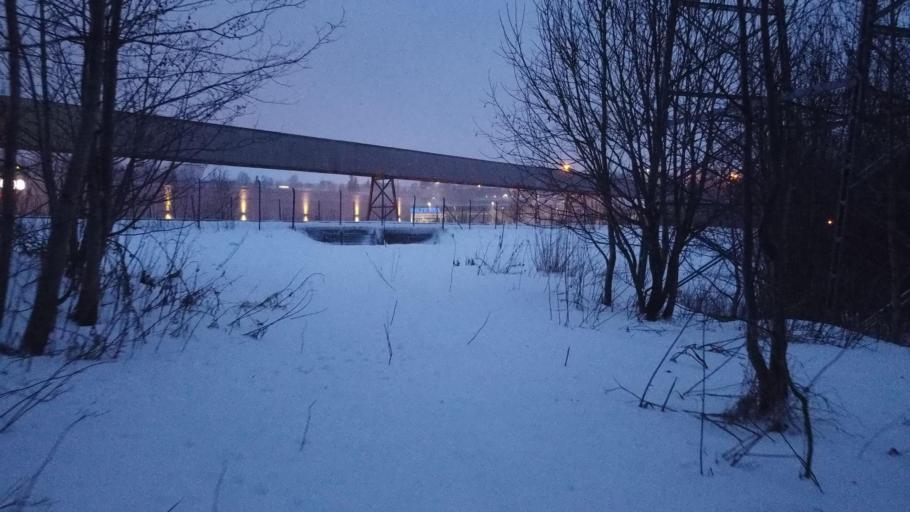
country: NO
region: Nordland
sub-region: Rana
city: Mo i Rana
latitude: 66.3225
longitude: 14.1695
